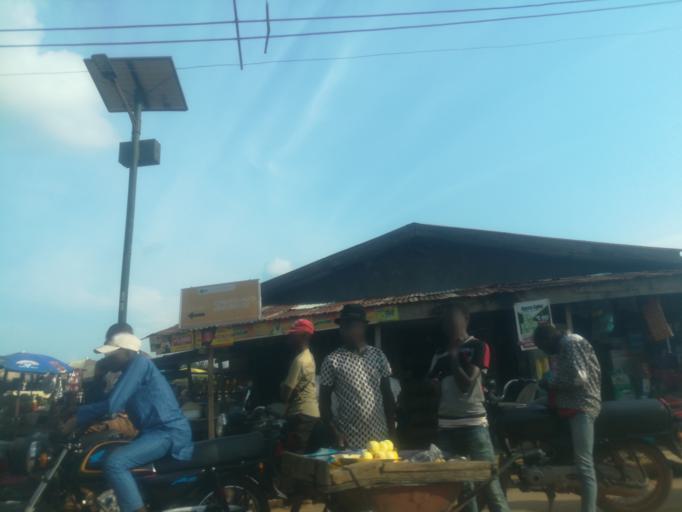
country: NG
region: Oyo
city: Ibadan
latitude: 7.3825
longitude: 3.8245
